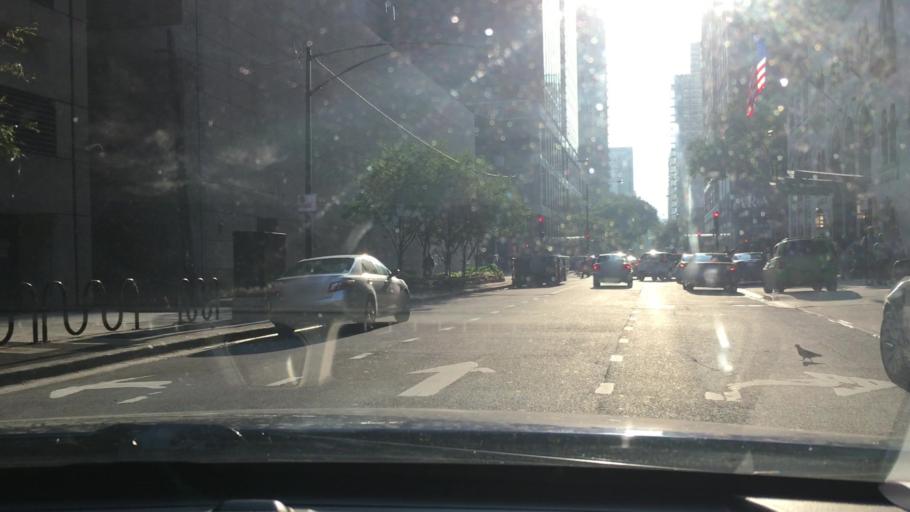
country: US
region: Illinois
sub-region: Cook County
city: Chicago
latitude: 41.8949
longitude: -87.6232
